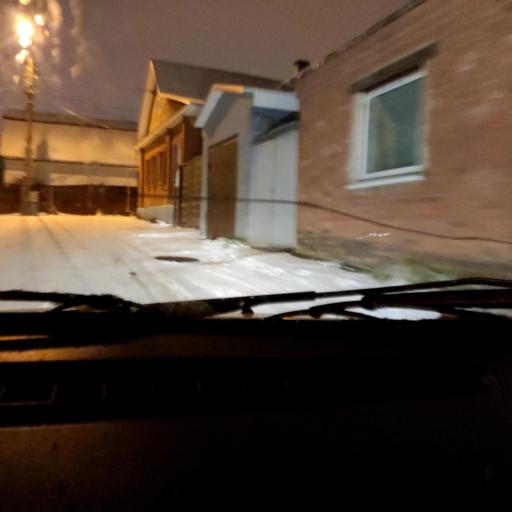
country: RU
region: Bashkortostan
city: Ufa
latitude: 54.7032
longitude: 55.9717
